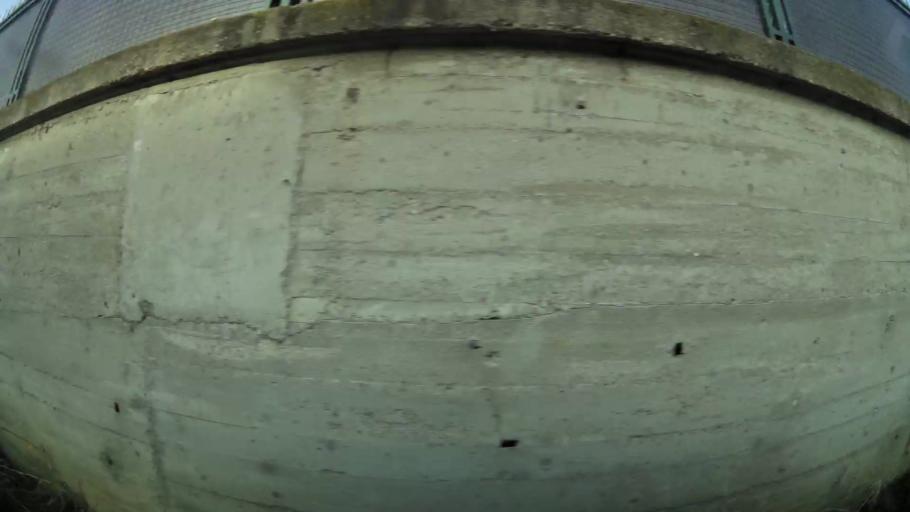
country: RS
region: Central Serbia
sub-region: Belgrade
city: Rakovica
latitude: 44.7367
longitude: 20.4549
